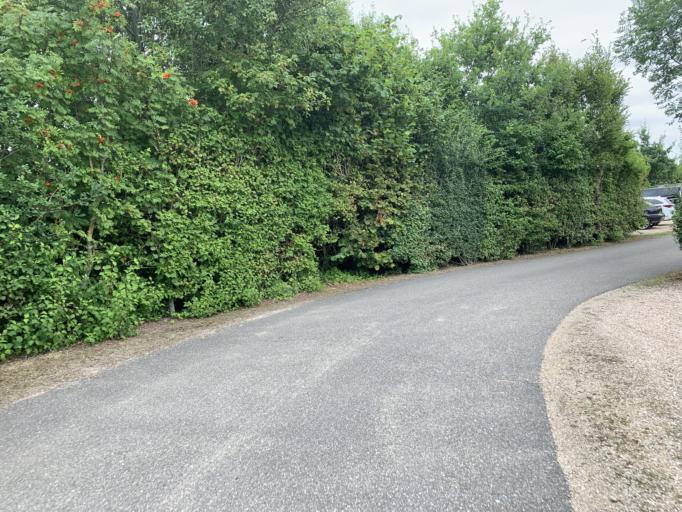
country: NL
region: Zeeland
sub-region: Gemeente Middelburg
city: Middelburg
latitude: 51.5544
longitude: 3.5542
